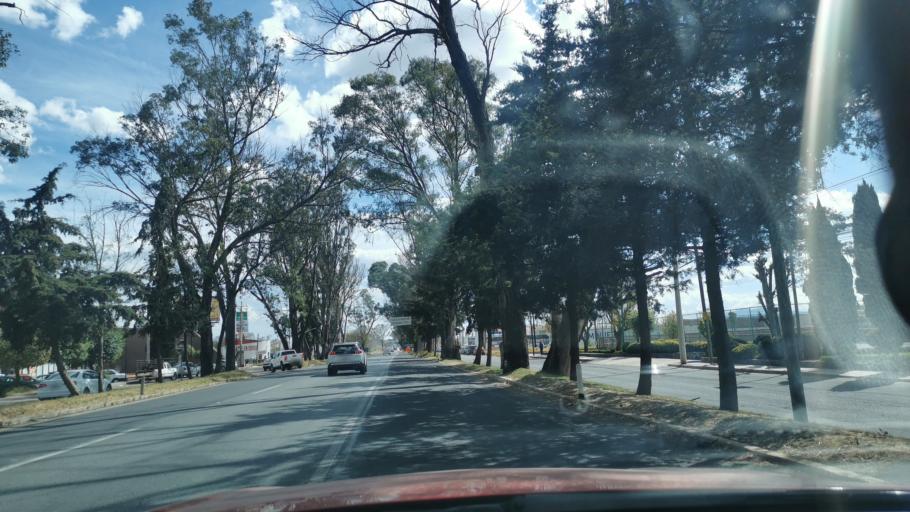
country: MX
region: Mexico
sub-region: Atlacomulco
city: Tecoac (Santa Maria Nativitas)
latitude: 19.7871
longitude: -99.8671
